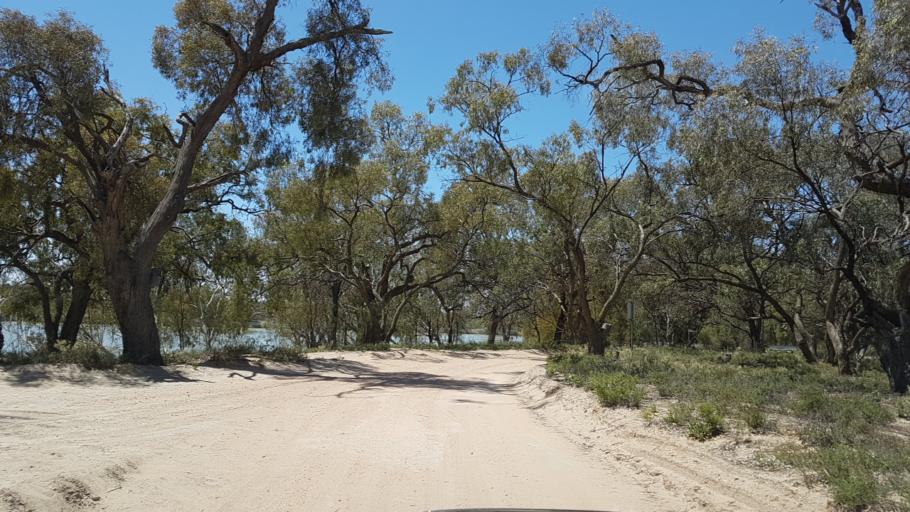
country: AU
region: South Australia
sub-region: Loxton Waikerie
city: Waikerie
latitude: -34.1623
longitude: 140.0329
